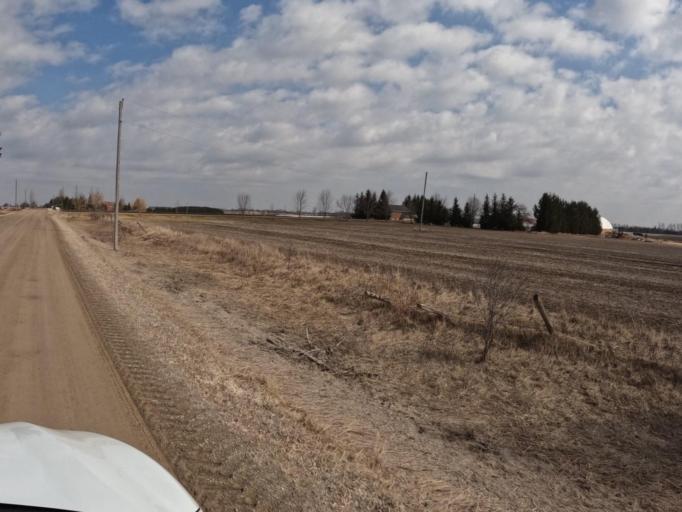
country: CA
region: Ontario
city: Orangeville
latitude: 43.9141
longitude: -80.2382
